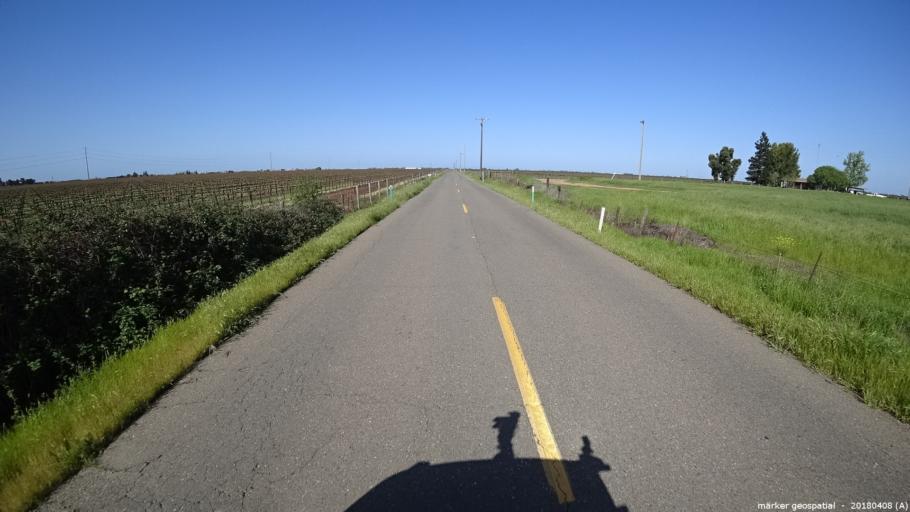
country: US
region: California
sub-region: Sacramento County
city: Elk Grove
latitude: 38.3617
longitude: -121.3626
